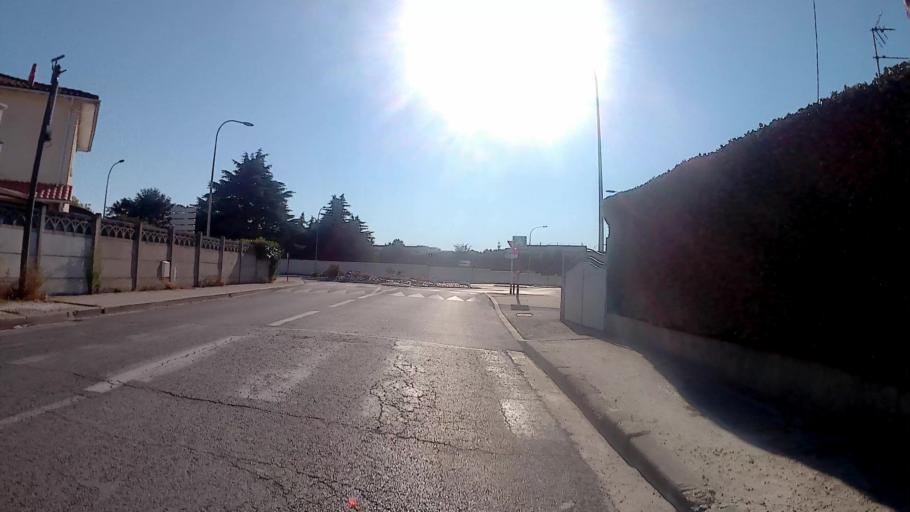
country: FR
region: Aquitaine
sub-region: Departement de la Gironde
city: Villenave-d'Ornon
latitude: 44.7808
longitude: -0.5575
